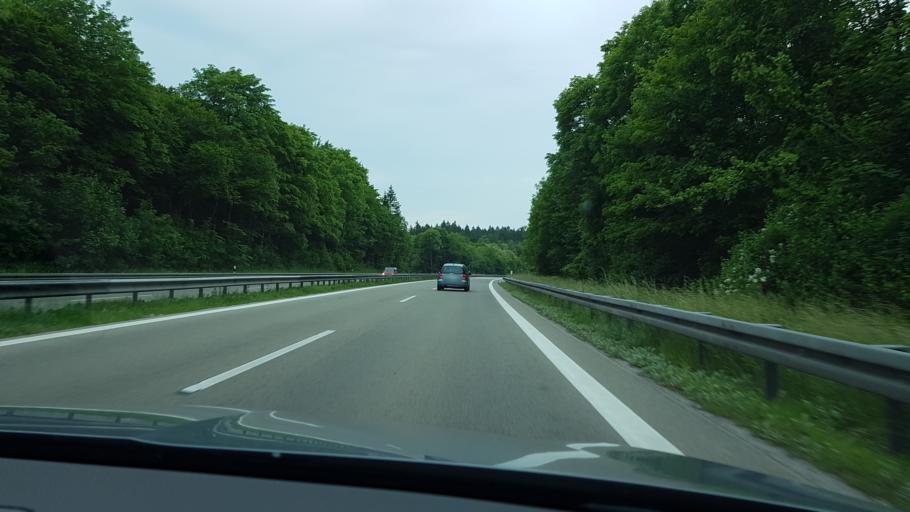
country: DE
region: Bavaria
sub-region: Upper Bavaria
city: Starnberg
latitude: 48.0068
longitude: 11.3993
